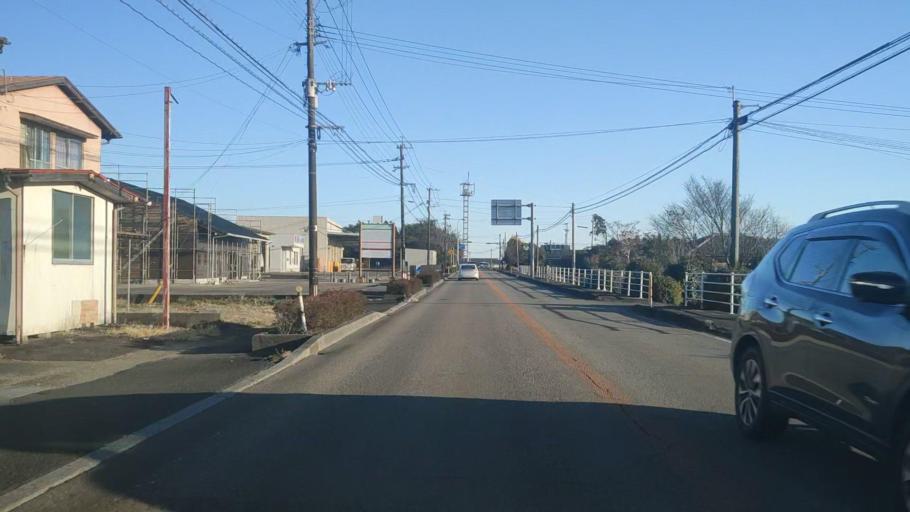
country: JP
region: Miyazaki
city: Takanabe
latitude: 32.1759
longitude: 131.5205
